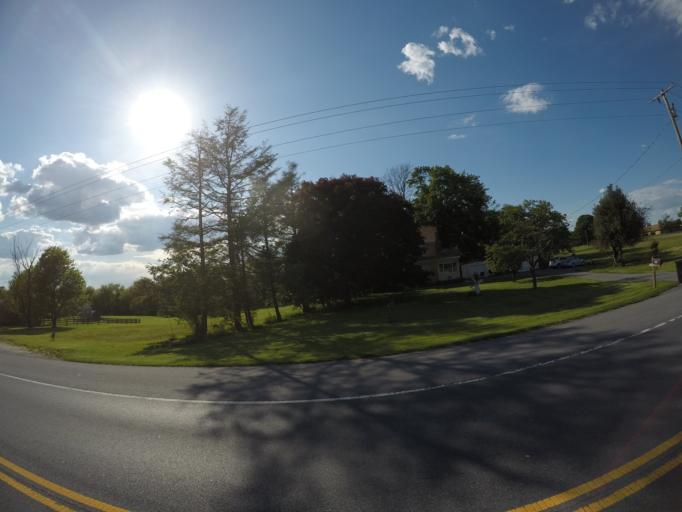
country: US
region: Maryland
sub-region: Carroll County
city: Mount Airy
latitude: 39.3469
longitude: -77.1732
